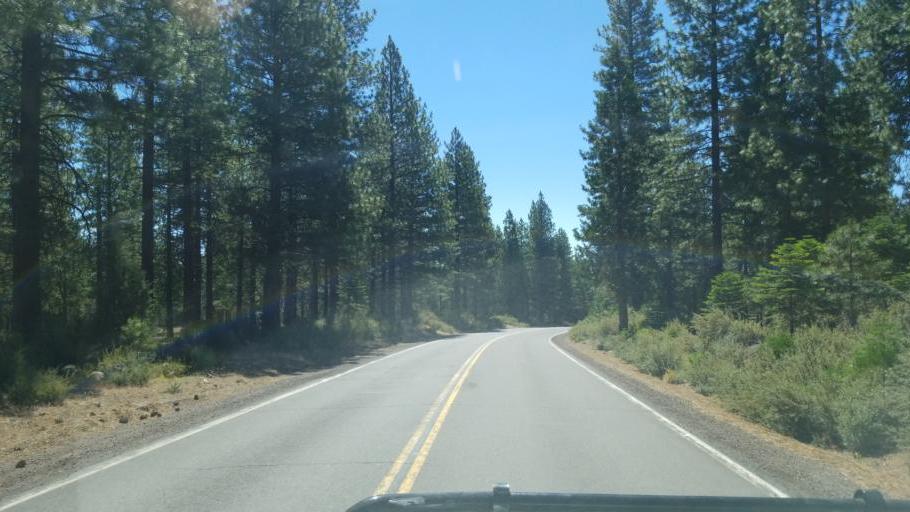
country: US
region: California
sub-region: Lassen County
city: Susanville
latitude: 40.4346
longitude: -120.7357
